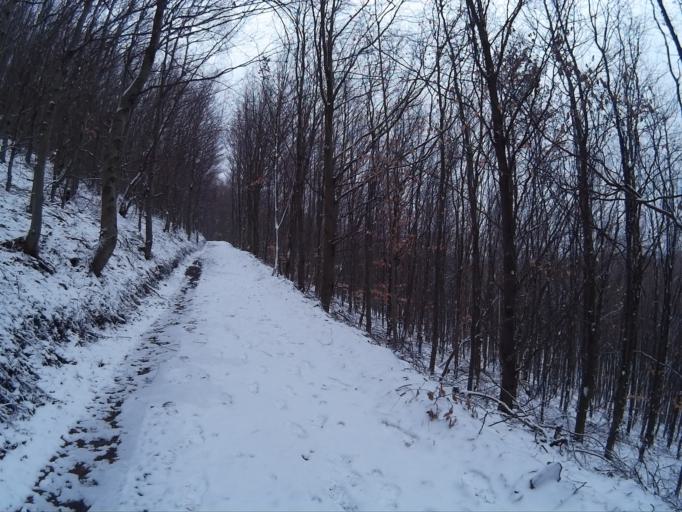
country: HU
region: Borsod-Abauj-Zemplen
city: Gonc
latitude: 48.5791
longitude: 21.4419
